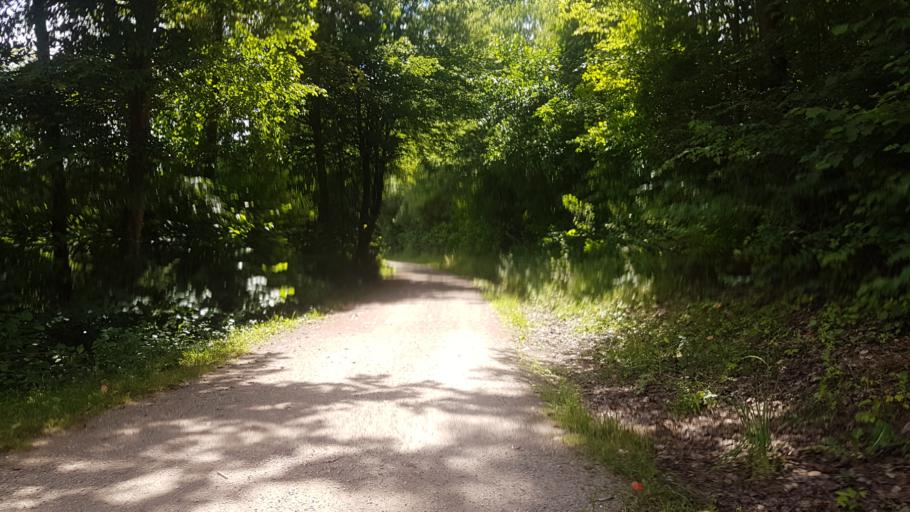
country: DE
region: Bavaria
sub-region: Regierungsbezirk Mittelfranken
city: Gunzenhausen
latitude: 49.1275
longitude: 10.7737
